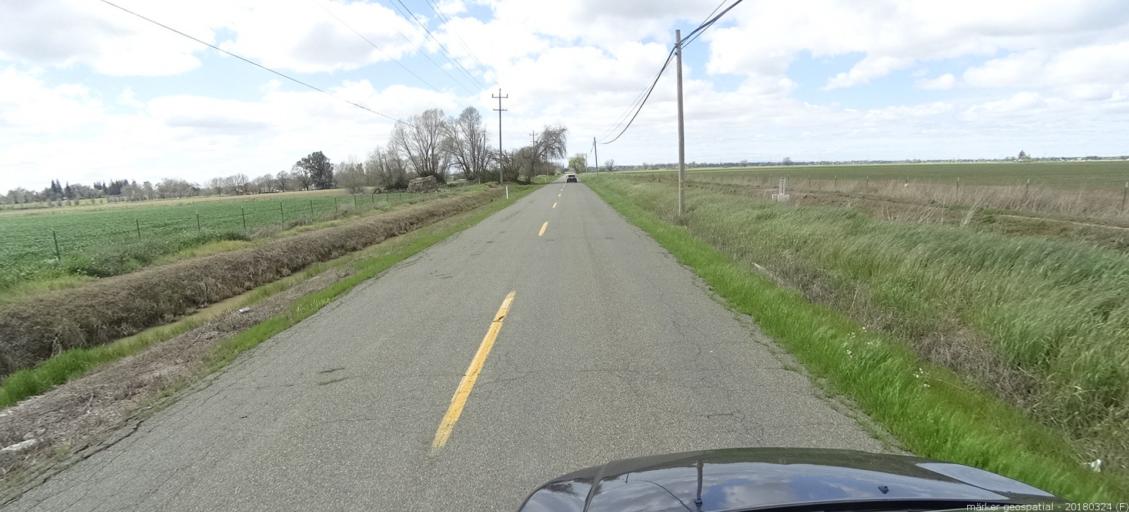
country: US
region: California
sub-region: Yolo County
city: West Sacramento
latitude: 38.6563
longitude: -121.5662
